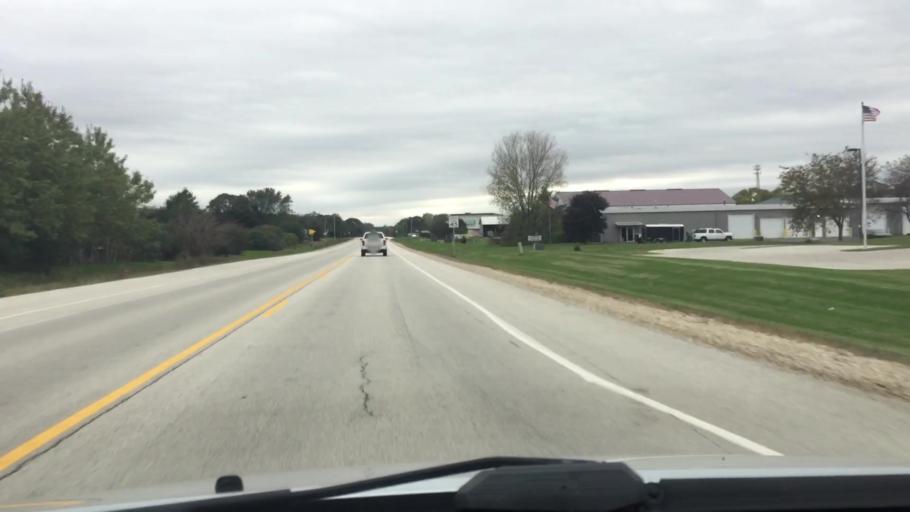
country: US
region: Wisconsin
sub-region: Waukesha County
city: North Prairie
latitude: 42.9386
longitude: -88.3886
